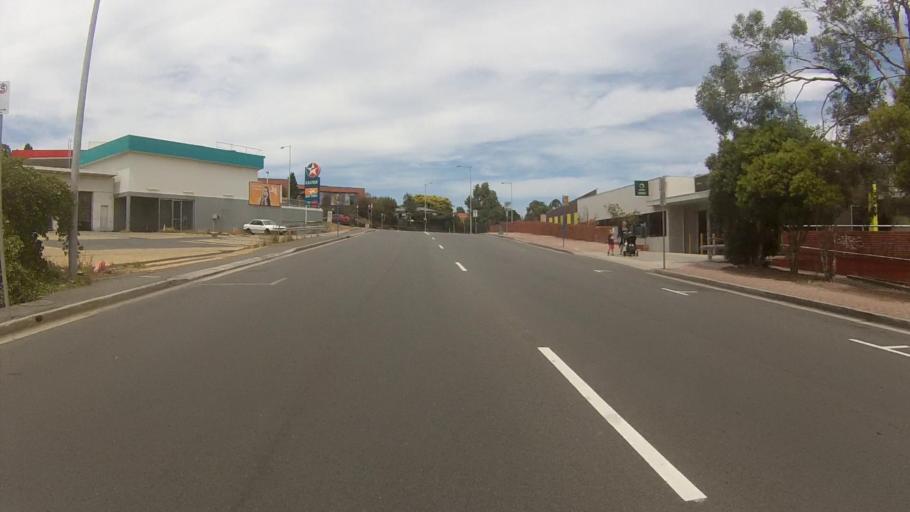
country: AU
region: Tasmania
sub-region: Clarence
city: Bellerive
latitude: -42.8656
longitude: 147.3725
